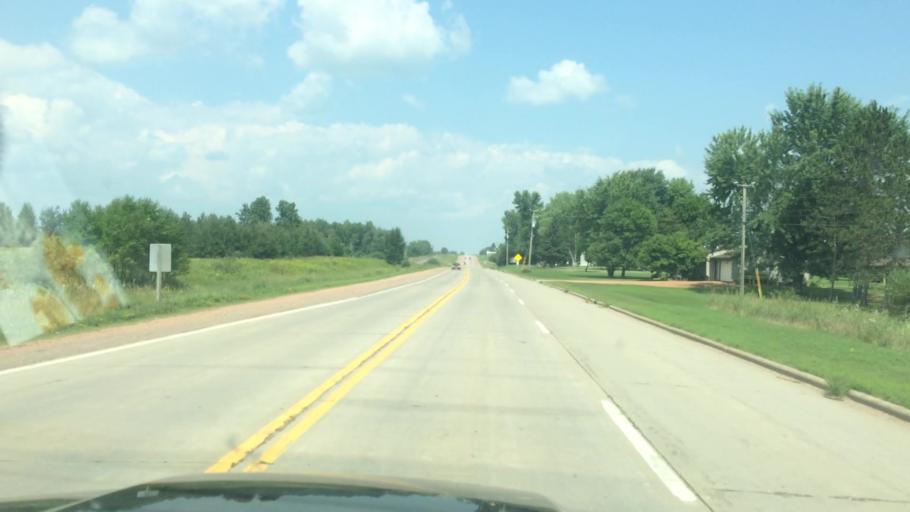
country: US
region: Wisconsin
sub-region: Clark County
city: Colby
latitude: 44.8543
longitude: -90.3159
